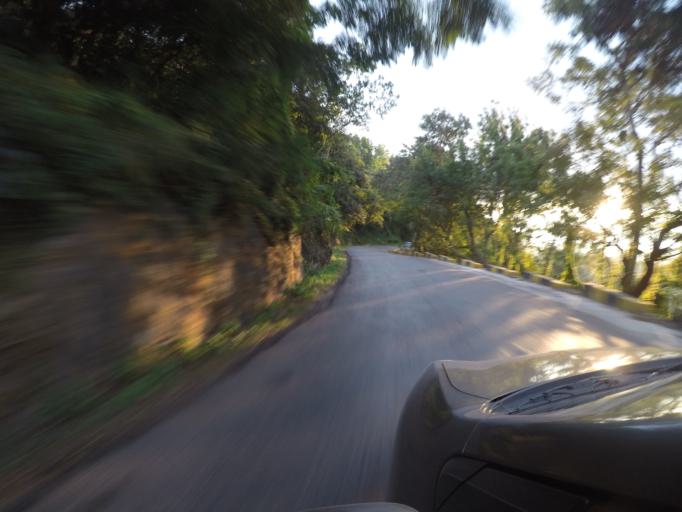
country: MM
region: Shan
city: Taunggyi
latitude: 20.8064
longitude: 97.0255
